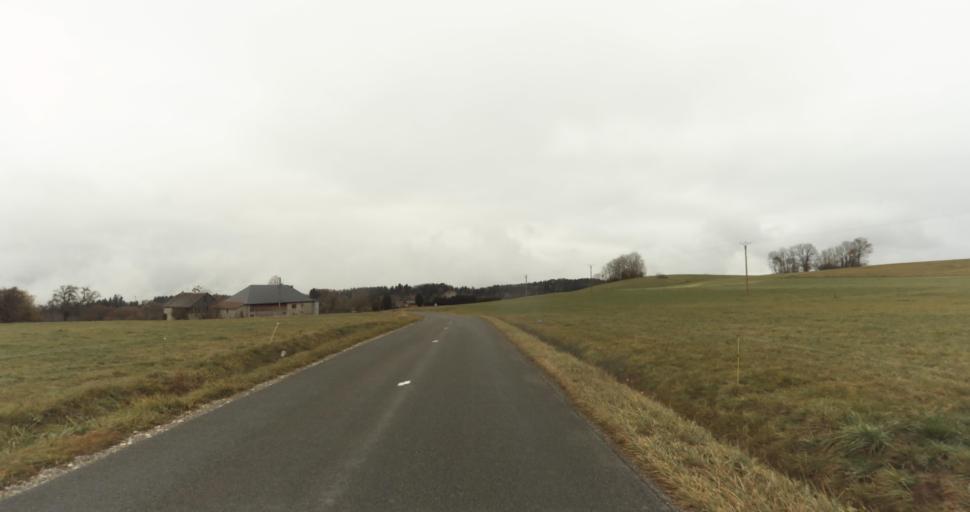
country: FR
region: Rhone-Alpes
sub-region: Departement de la Haute-Savoie
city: Groisy
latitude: 46.0349
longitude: 6.1855
